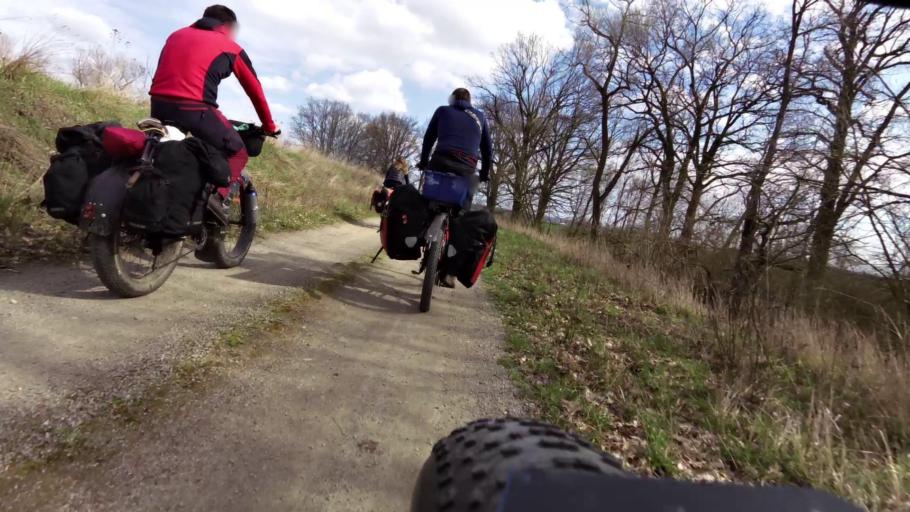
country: DE
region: Brandenburg
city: Lebus
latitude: 52.4362
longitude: 14.5729
